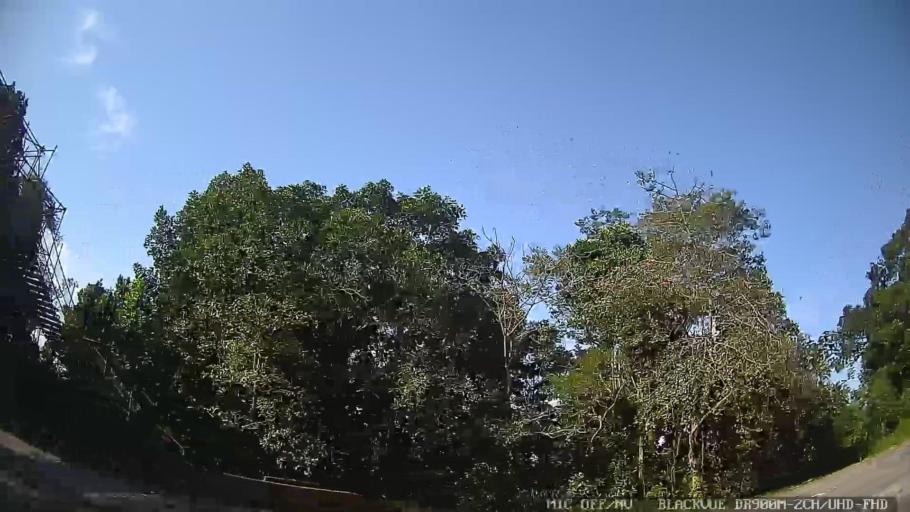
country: BR
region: Sao Paulo
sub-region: Cubatao
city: Cubatao
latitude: -23.8925
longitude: -46.4708
